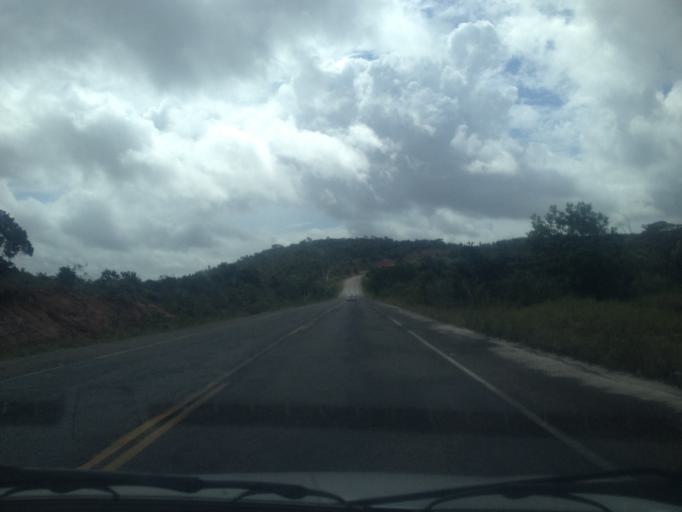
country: BR
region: Bahia
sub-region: Conde
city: Conde
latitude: -12.0898
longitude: -37.7736
